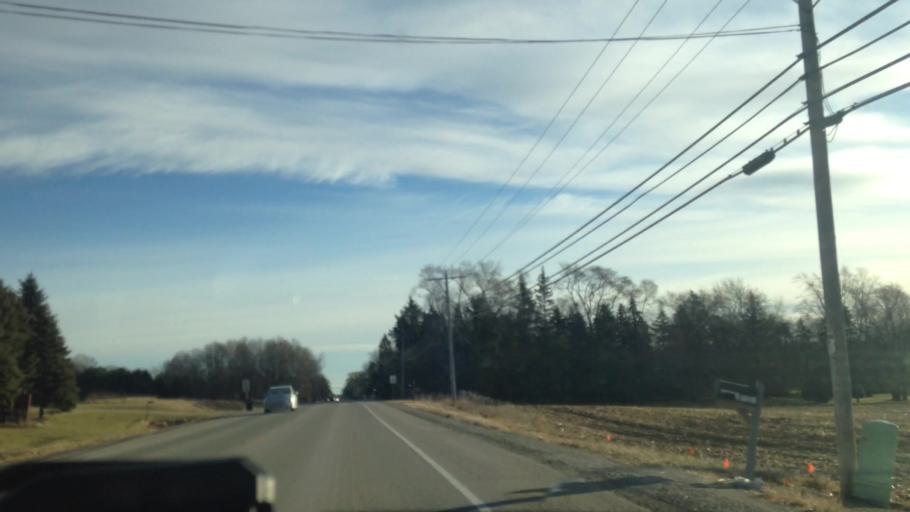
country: US
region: Wisconsin
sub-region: Ozaukee County
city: Cedarburg
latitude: 43.2932
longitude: -88.0305
